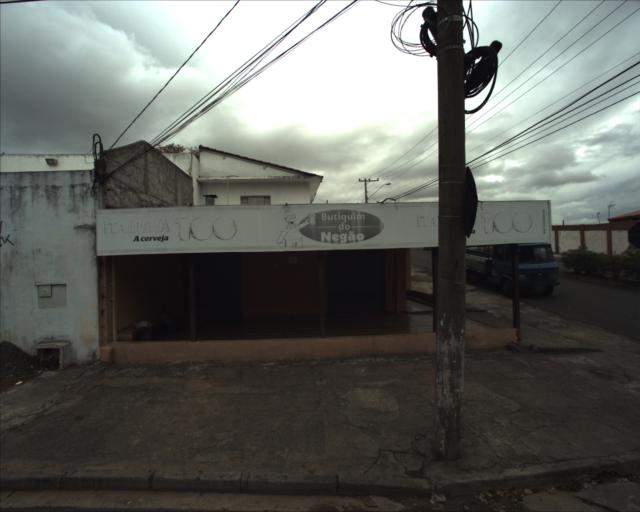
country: BR
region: Sao Paulo
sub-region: Sorocaba
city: Sorocaba
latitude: -23.4774
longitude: -47.4716
